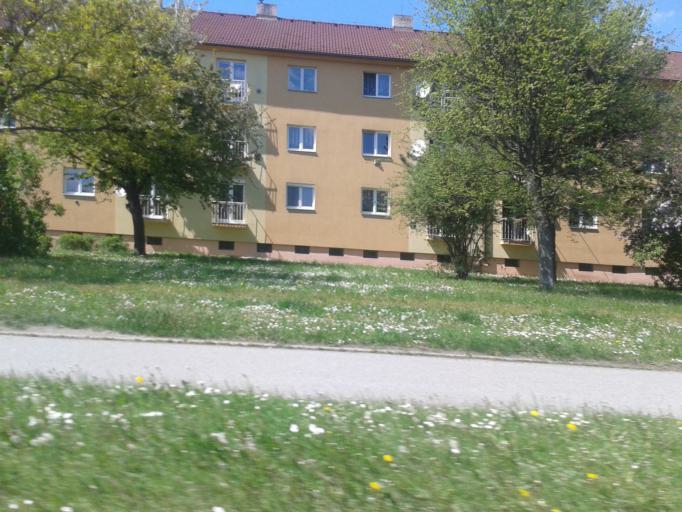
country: CZ
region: Central Bohemia
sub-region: Okres Beroun
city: Beroun
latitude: 49.9566
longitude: 14.0562
